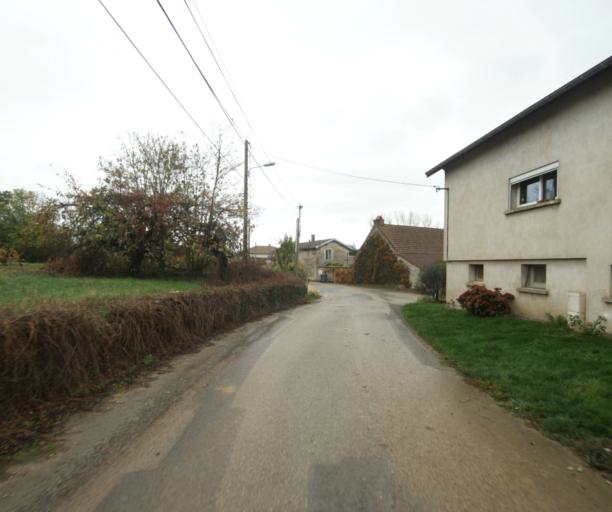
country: FR
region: Rhone-Alpes
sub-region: Departement de l'Ain
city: Pont-de-Vaux
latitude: 46.4829
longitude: 4.8650
